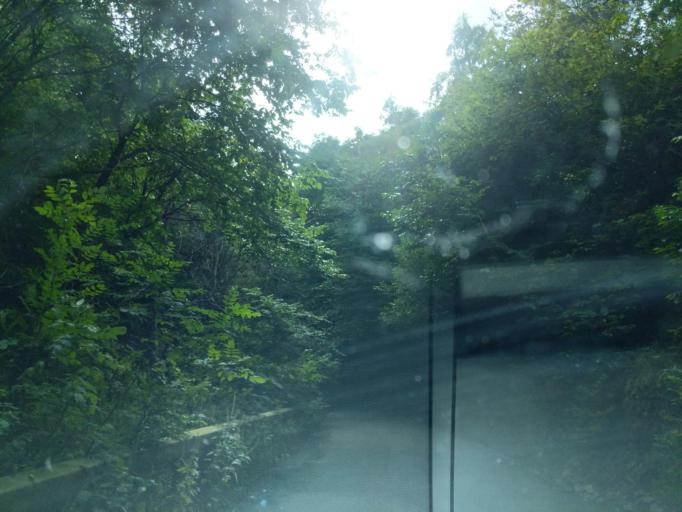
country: GB
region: Scotland
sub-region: Midlothian
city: Loanhead
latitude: 55.8722
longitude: -3.1420
